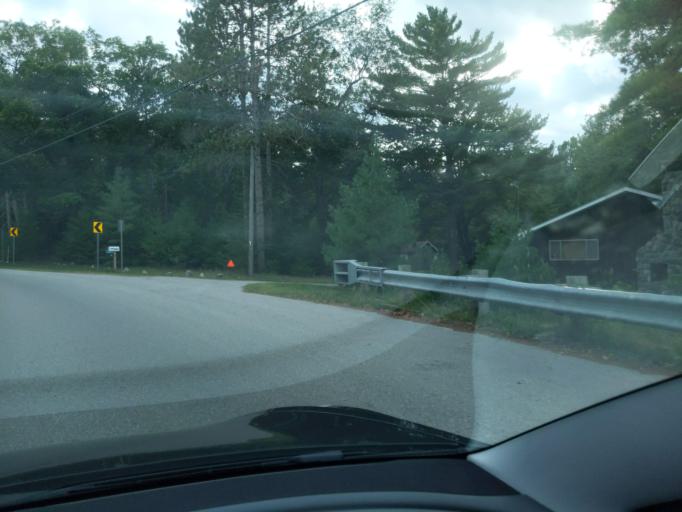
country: US
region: Michigan
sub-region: Kalkaska County
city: Rapid City
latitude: 44.8454
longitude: -85.3075
